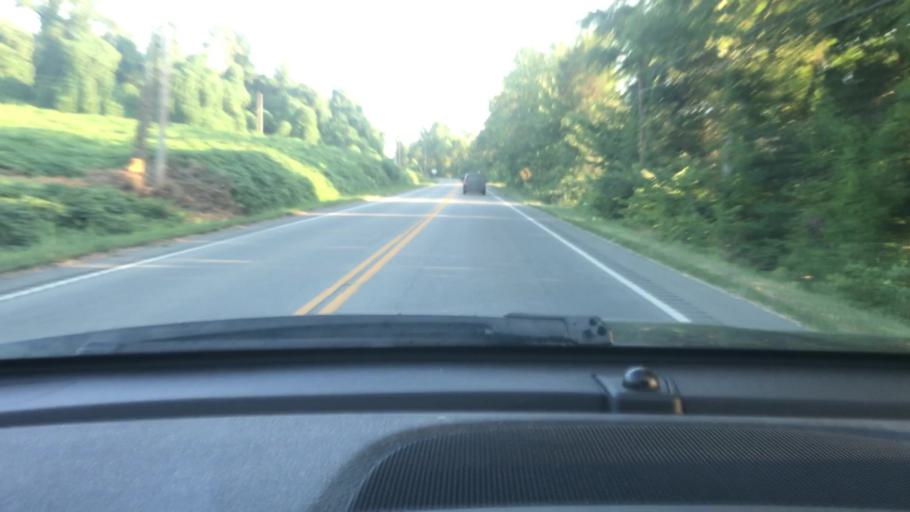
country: US
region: Tennessee
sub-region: Dickson County
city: Charlotte
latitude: 36.1579
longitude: -87.3560
